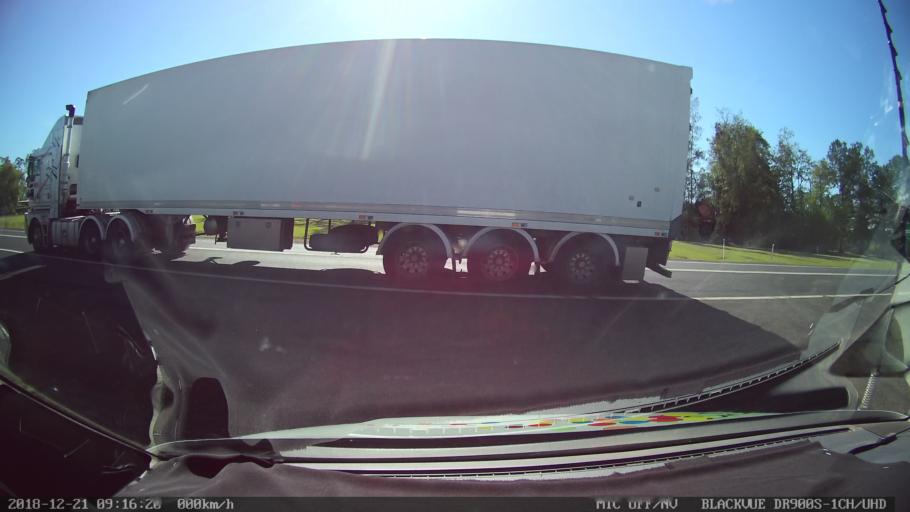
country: AU
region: New South Wales
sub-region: Clarence Valley
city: Maclean
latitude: -29.2825
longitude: 152.9893
